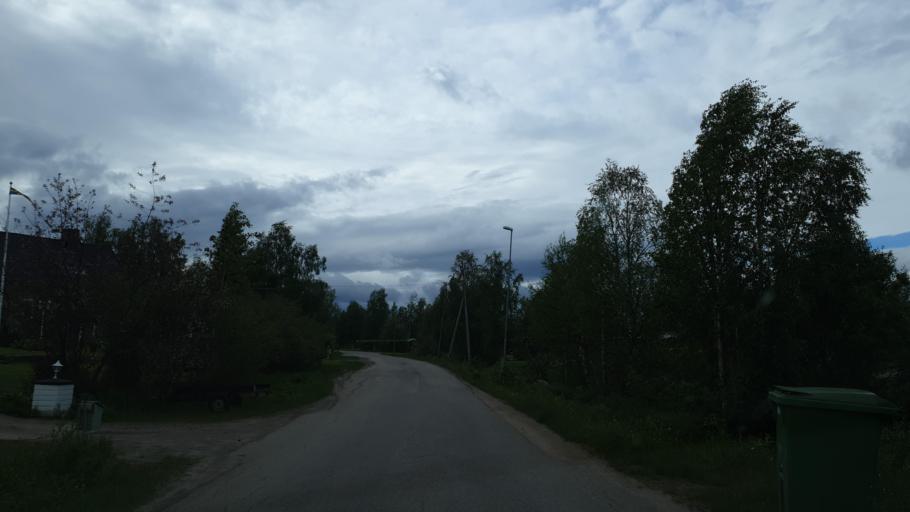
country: SE
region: Norrbotten
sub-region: Gallivare Kommun
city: Gaellivare
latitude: 67.1316
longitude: 20.6414
